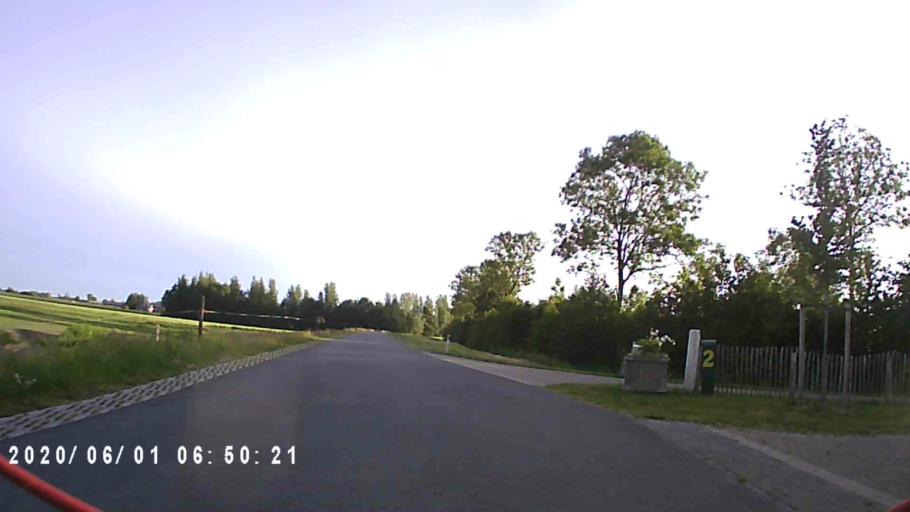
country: NL
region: Friesland
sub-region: Gemeente Kollumerland en Nieuwkruisland
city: Kollum
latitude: 53.3019
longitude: 6.1307
